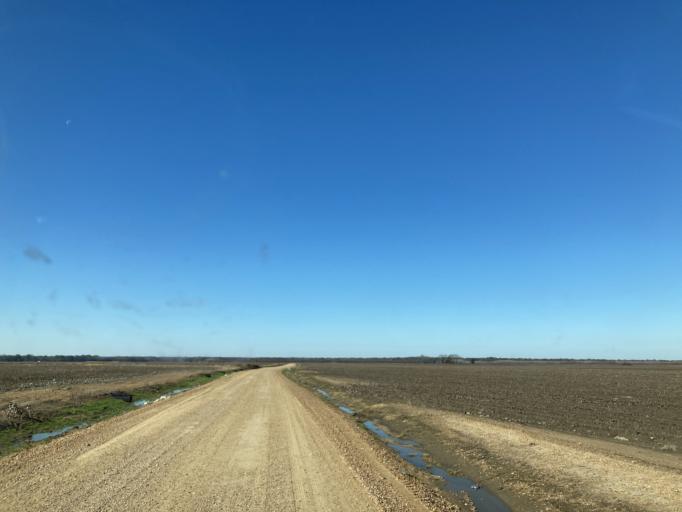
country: US
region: Mississippi
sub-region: Sharkey County
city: Rolling Fork
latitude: 32.8229
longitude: -90.7317
